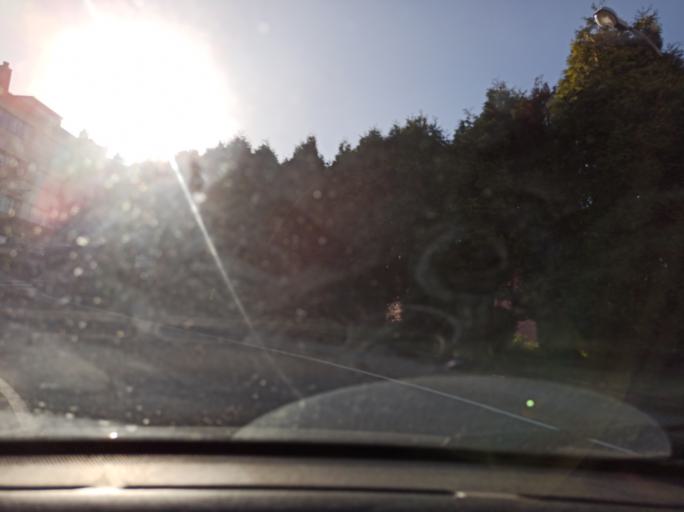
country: ES
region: Galicia
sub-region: Provincia da Coruna
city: A Coruna
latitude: 43.3295
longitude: -8.3995
